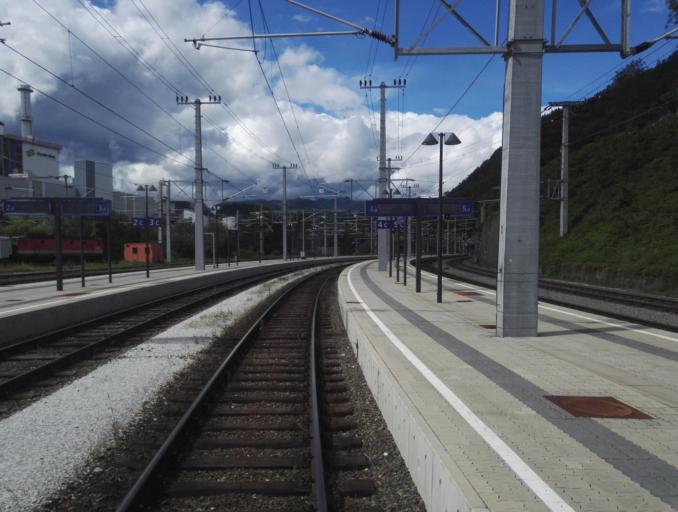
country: AT
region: Styria
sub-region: Politischer Bezirk Bruck-Muerzzuschlag
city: Bruck an der Mur
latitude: 47.4146
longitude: 15.2792
